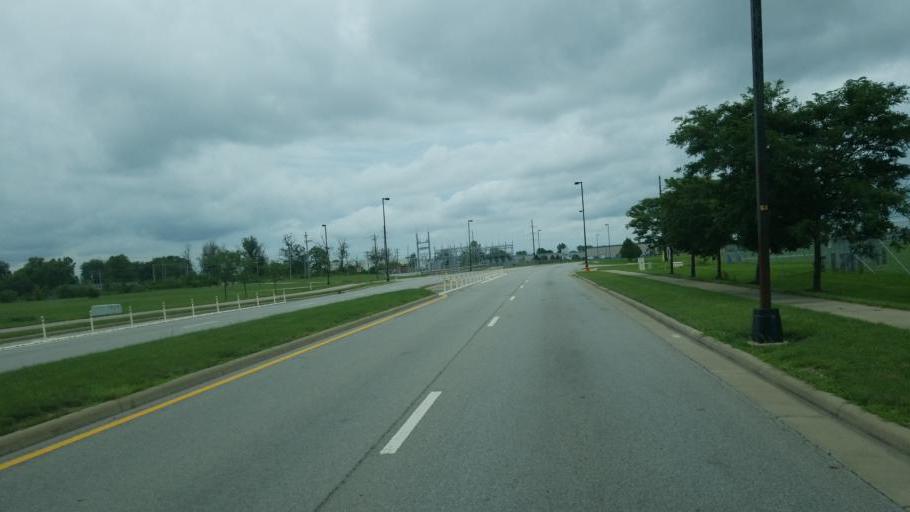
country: US
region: Ohio
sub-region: Franklin County
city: Obetz
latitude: 39.8209
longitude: -82.9463
